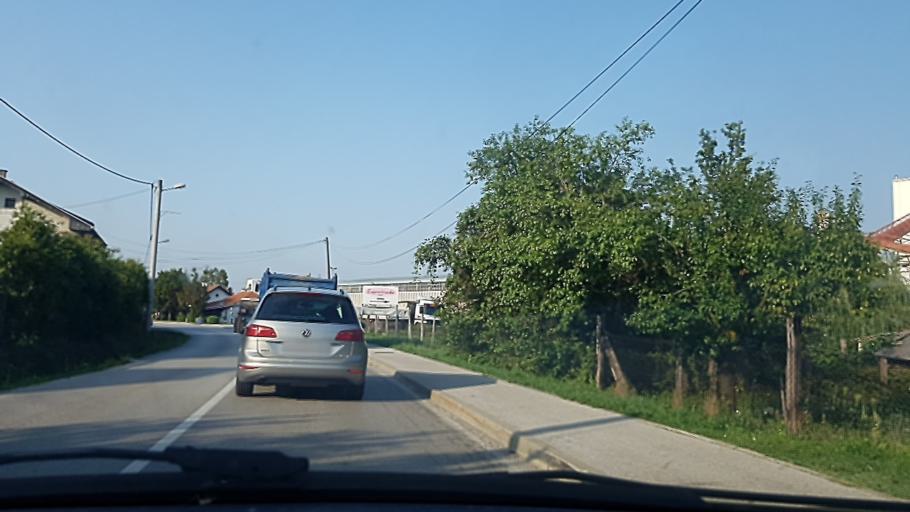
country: HR
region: Zagrebacka
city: Pojatno
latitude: 45.9081
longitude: 15.8071
